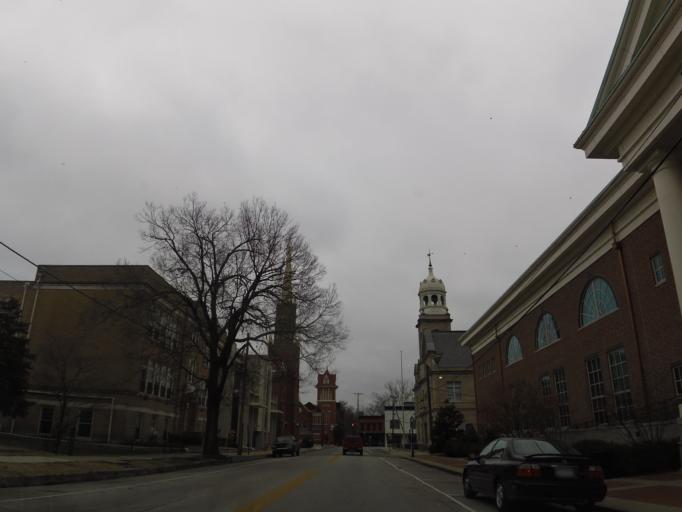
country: US
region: Kentucky
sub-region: Franklin County
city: Frankfort
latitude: 38.1980
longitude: -84.8800
